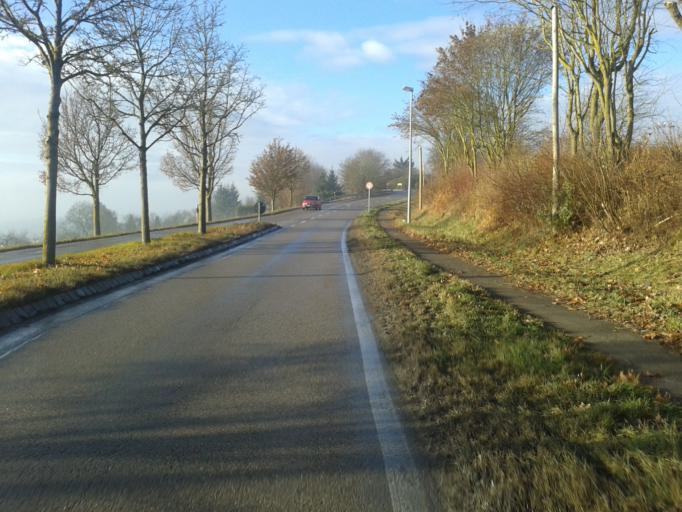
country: DE
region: Baden-Wuerttemberg
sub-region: Tuebingen Region
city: Erbach
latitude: 48.3763
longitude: 9.8902
